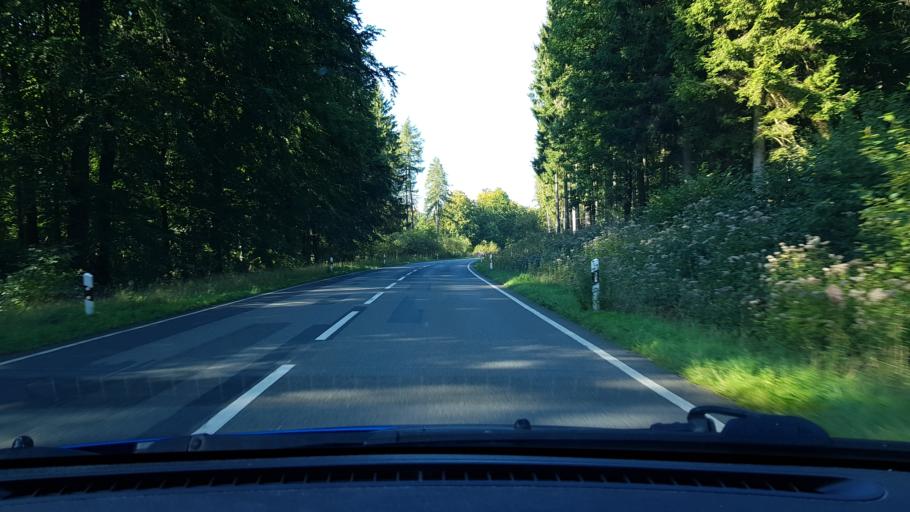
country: DE
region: Lower Saxony
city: Egestorf
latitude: 52.2703
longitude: 9.4876
